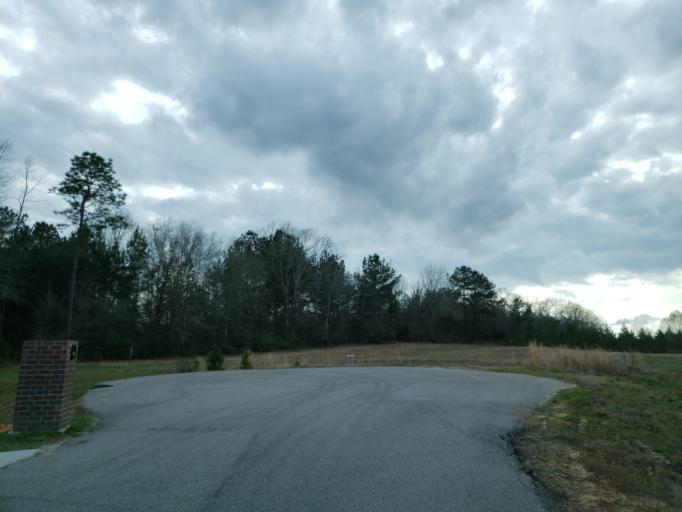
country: US
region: Mississippi
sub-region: Jones County
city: Ellisville
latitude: 31.5617
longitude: -89.2487
